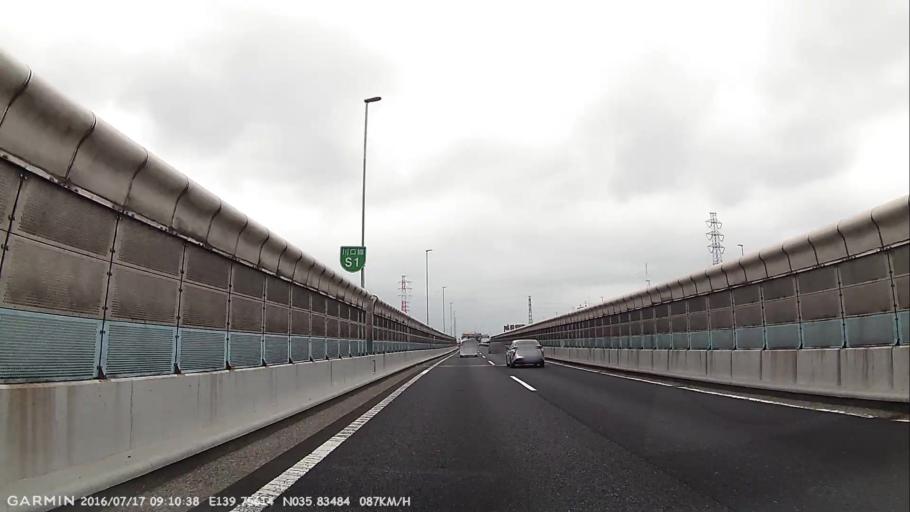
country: JP
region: Saitama
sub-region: Kawaguchi-shi
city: Hatogaya-honcho
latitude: 35.8349
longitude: 139.7561
